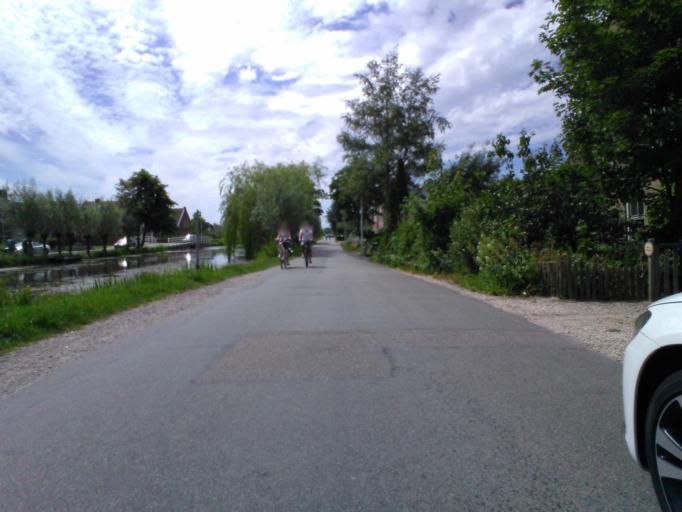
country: NL
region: South Holland
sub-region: Molenwaard
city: Liesveld
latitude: 51.8770
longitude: 4.8222
